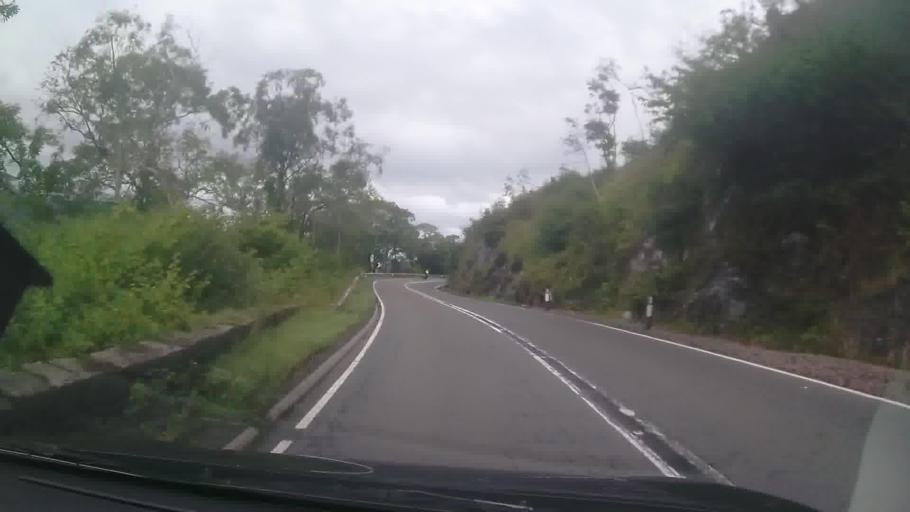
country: GB
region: Scotland
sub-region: Highland
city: Fort William
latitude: 56.7360
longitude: -5.2143
